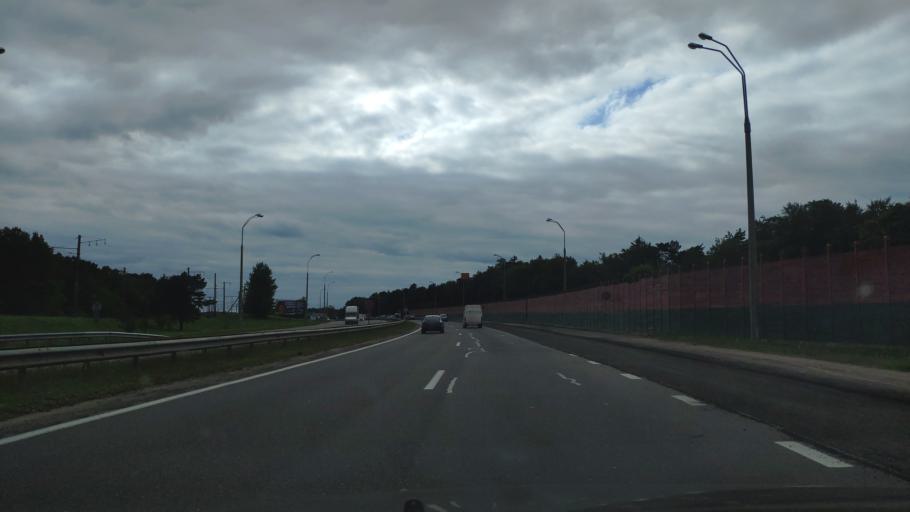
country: BY
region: Minsk
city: Zhdanovichy
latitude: 53.9525
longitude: 27.4074
